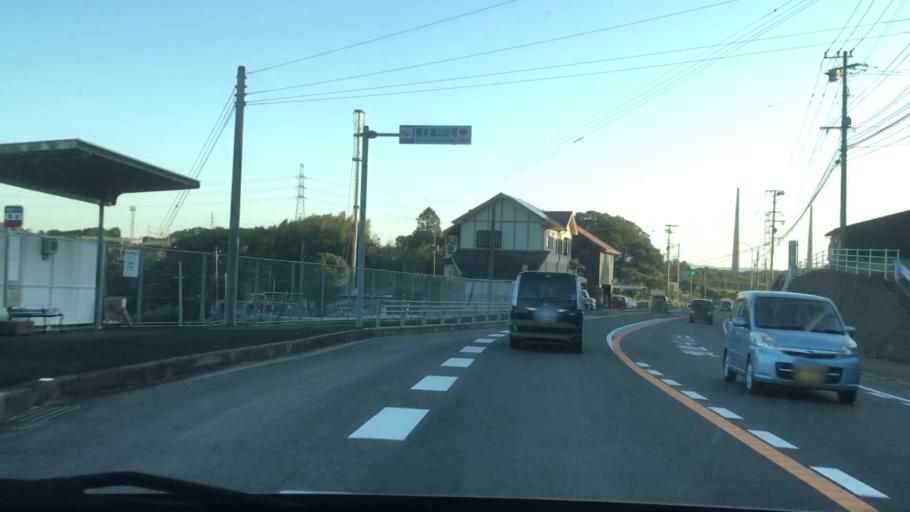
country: JP
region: Nagasaki
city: Sasebo
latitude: 33.0801
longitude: 129.7560
